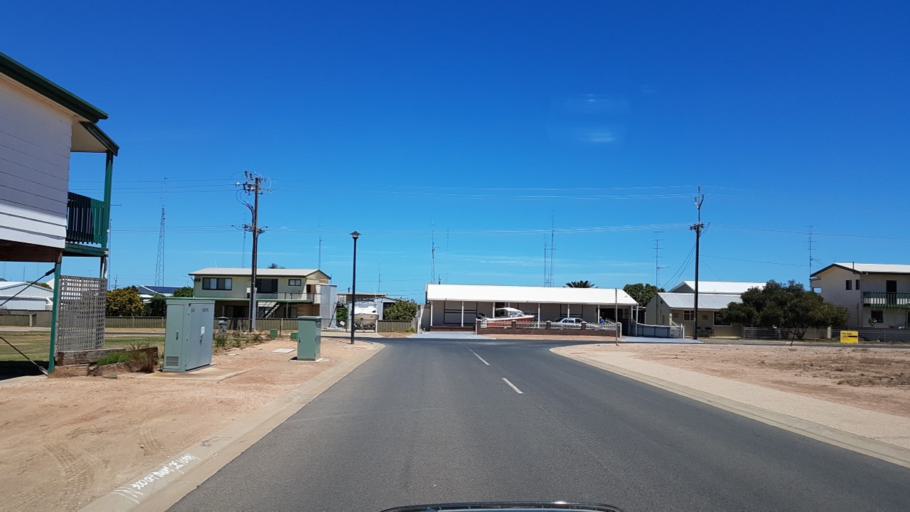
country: AU
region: South Australia
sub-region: Copper Coast
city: Wallaroo
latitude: -33.8951
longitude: 137.6298
